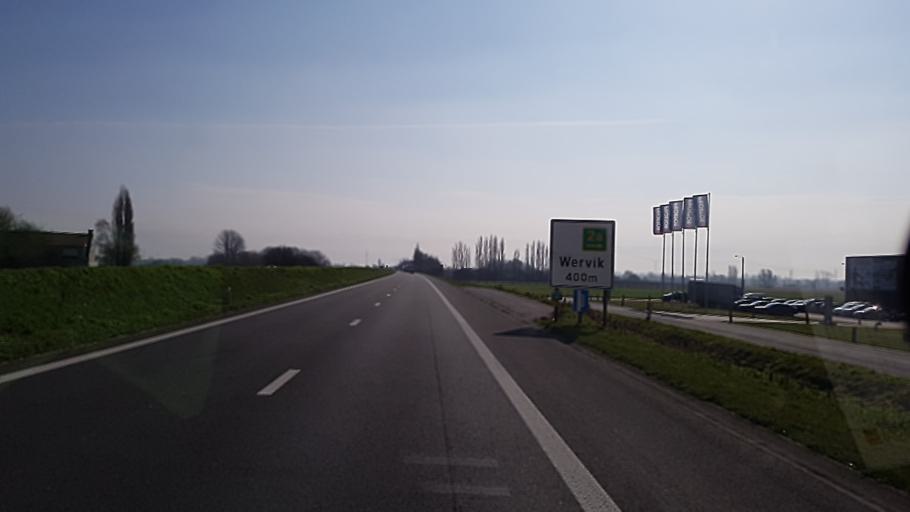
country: BE
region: Flanders
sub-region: Provincie West-Vlaanderen
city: Menen
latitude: 50.8191
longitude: 3.0830
